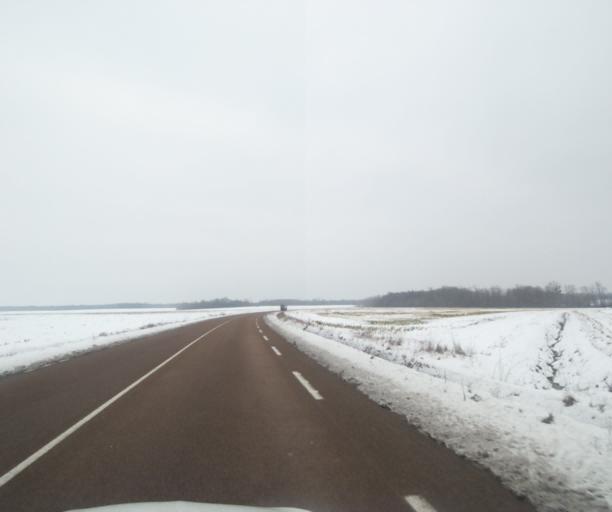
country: FR
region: Champagne-Ardenne
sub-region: Departement de la Haute-Marne
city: Saint-Dizier
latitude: 48.5928
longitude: 4.8914
